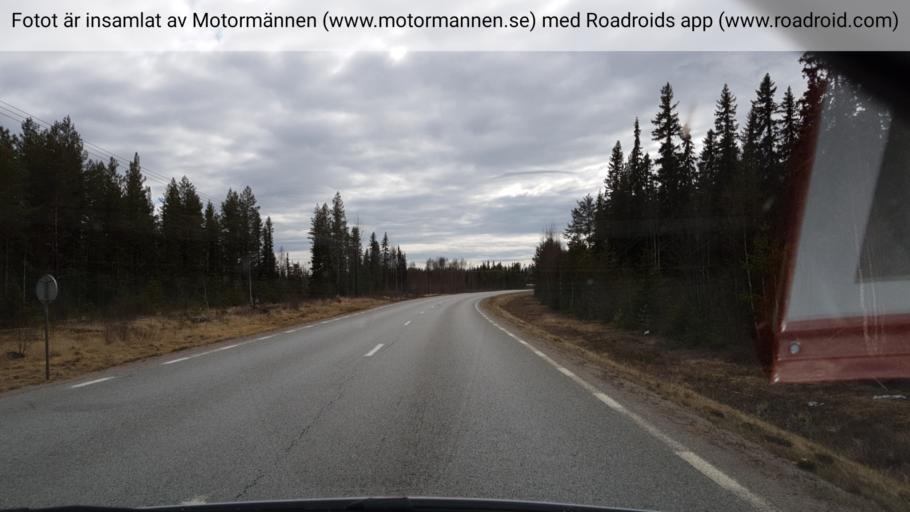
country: SE
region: Vaesterbotten
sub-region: Asele Kommun
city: Asele
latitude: 63.7549
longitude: 17.0127
